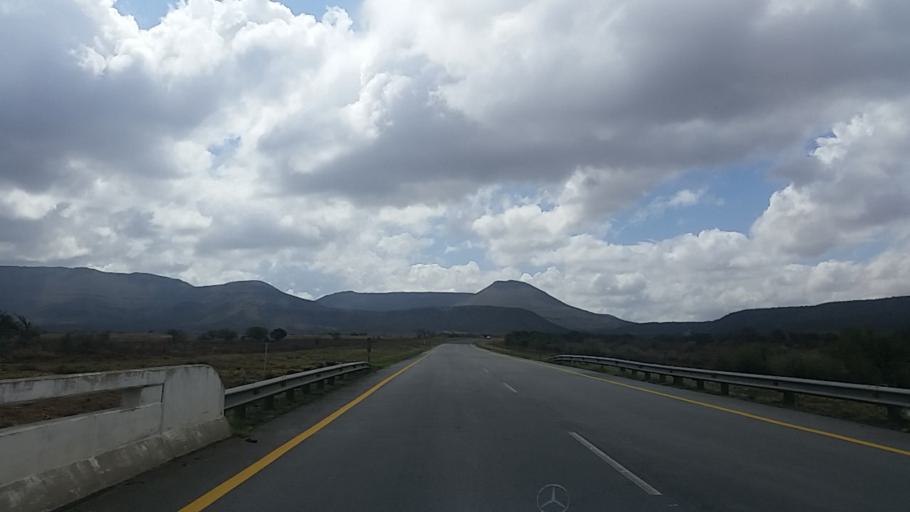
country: ZA
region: Eastern Cape
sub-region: Cacadu District Municipality
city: Graaff-Reinet
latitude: -32.0862
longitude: 24.6026
